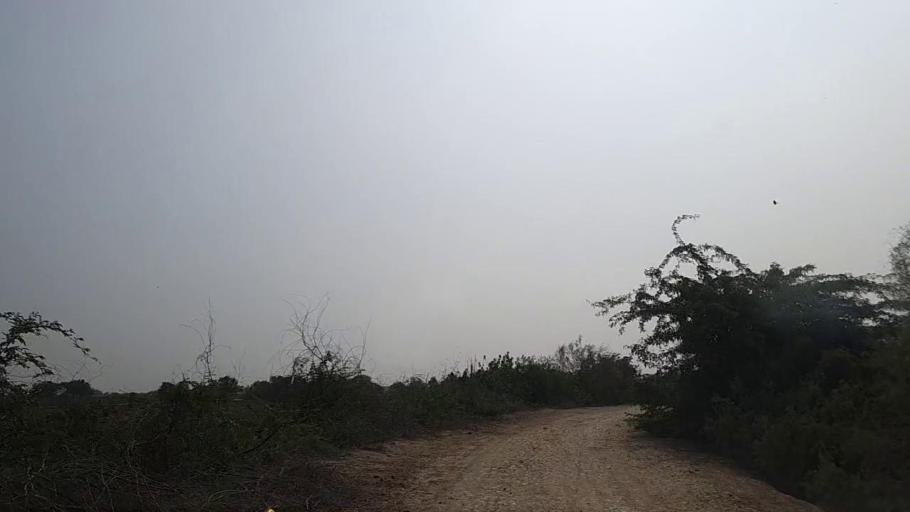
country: PK
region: Sindh
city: Mirpur Sakro
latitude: 24.6009
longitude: 67.7192
